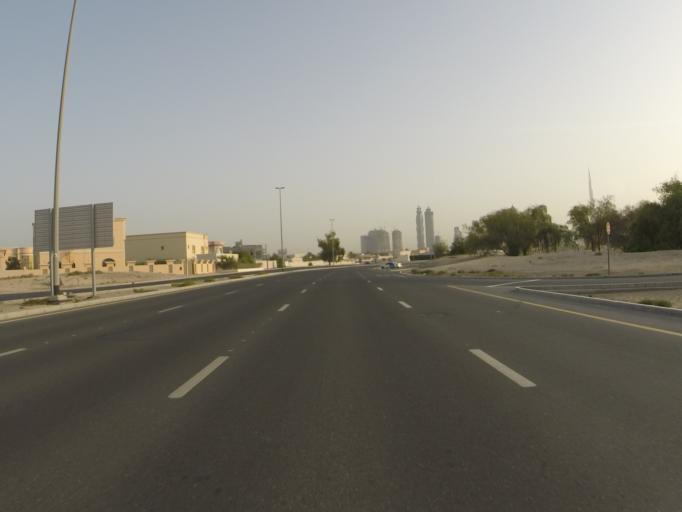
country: AE
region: Dubai
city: Dubai
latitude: 25.1605
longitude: 55.2568
